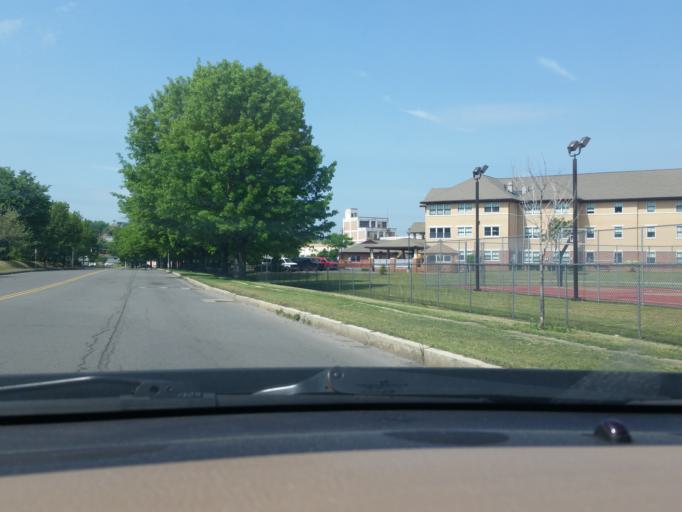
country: US
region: Pennsylvania
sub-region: Luzerne County
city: Wilkes-Barre
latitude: 41.2387
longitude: -75.8846
